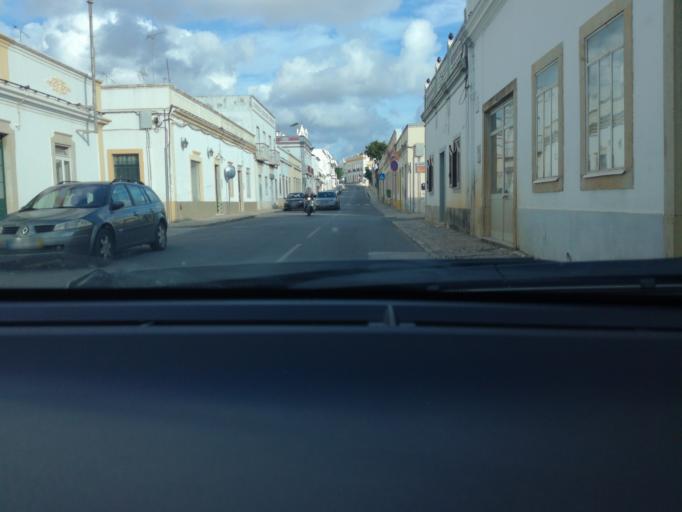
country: PT
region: Faro
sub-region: Sao Bras de Alportel
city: Sao Bras de Alportel
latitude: 37.0942
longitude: -7.8975
